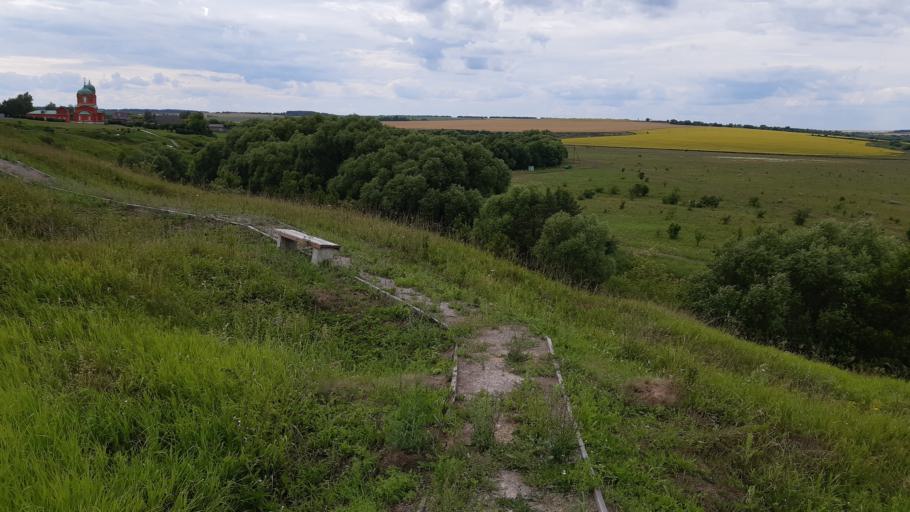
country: RU
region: Tula
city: Yepifan'
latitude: 53.6700
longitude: 38.6503
